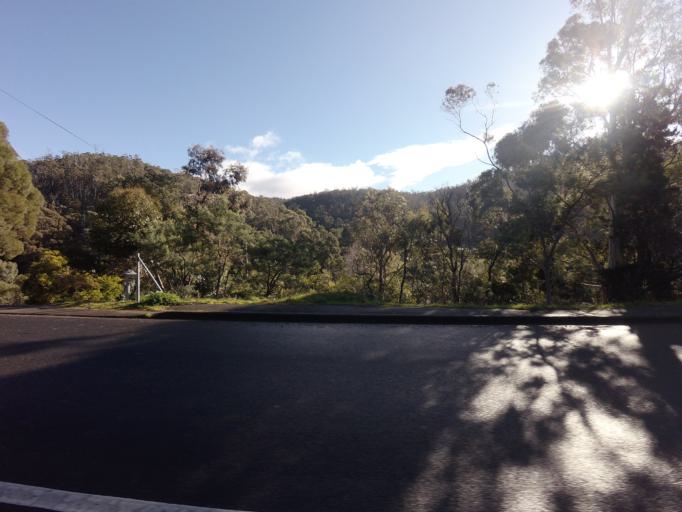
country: AU
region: Tasmania
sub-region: Glenorchy
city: Berriedale
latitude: -42.8157
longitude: 147.2277
